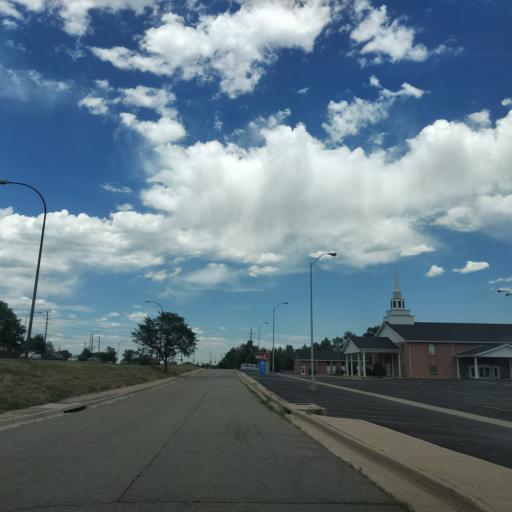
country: US
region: Colorado
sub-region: Jefferson County
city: Lakewood
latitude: 39.7076
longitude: -105.1093
